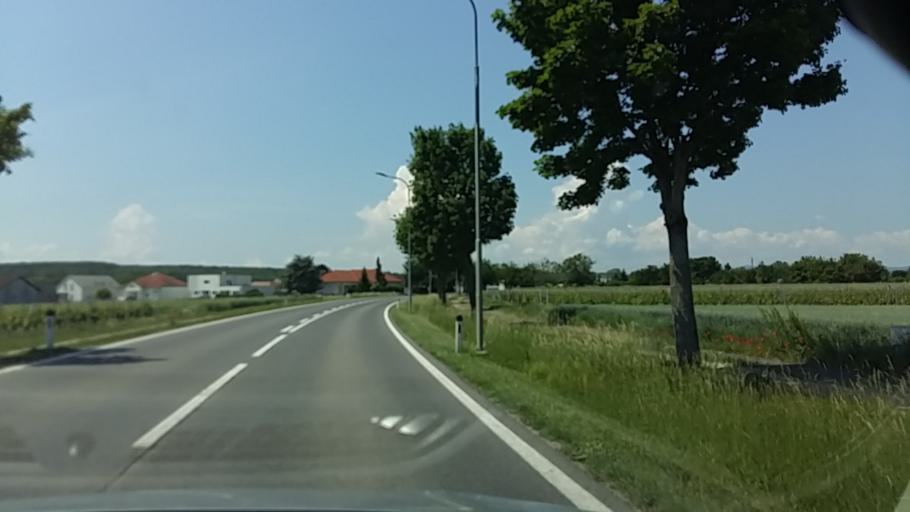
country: AT
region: Burgenland
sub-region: Politischer Bezirk Oberpullendorf
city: Horitschon
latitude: 47.5940
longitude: 16.5894
